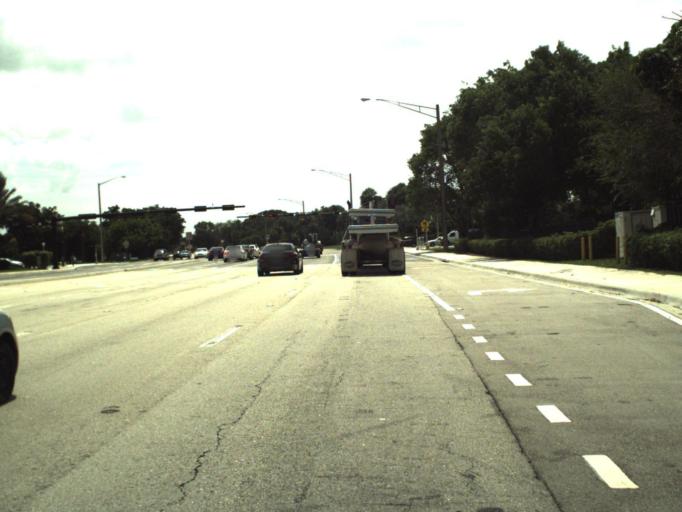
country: US
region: Florida
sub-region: Broward County
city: Tamarac
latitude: 26.2377
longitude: -80.2463
